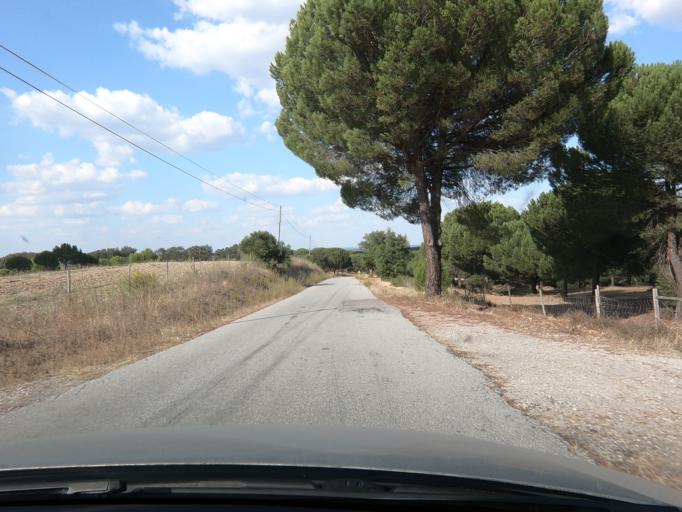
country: PT
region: Setubal
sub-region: Alcacer do Sal
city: Alcacer do Sal
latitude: 38.2430
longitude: -8.3642
